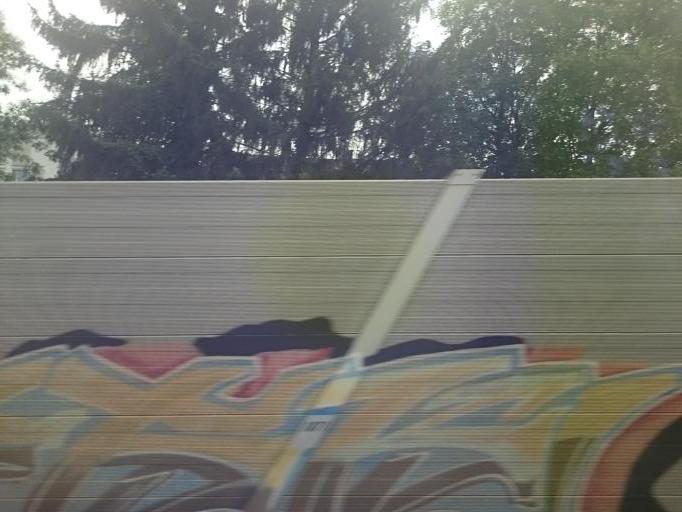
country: DE
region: Bavaria
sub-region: Upper Bavaria
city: Munich
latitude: 48.1166
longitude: 11.5691
